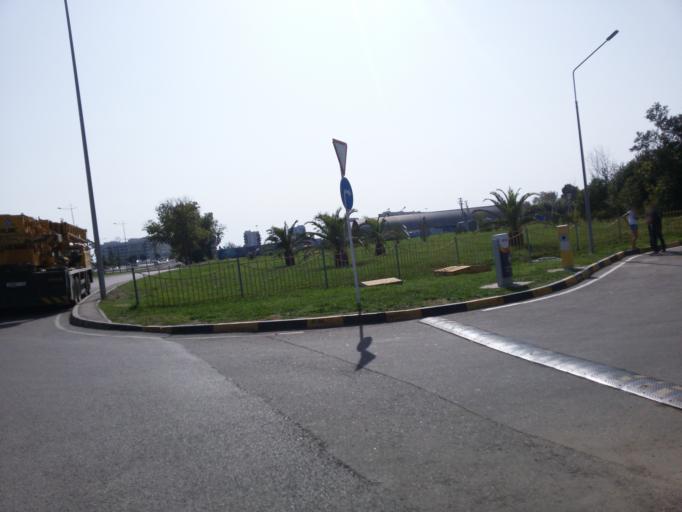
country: RU
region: Krasnodarskiy
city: Adler
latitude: 43.4170
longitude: 39.9400
